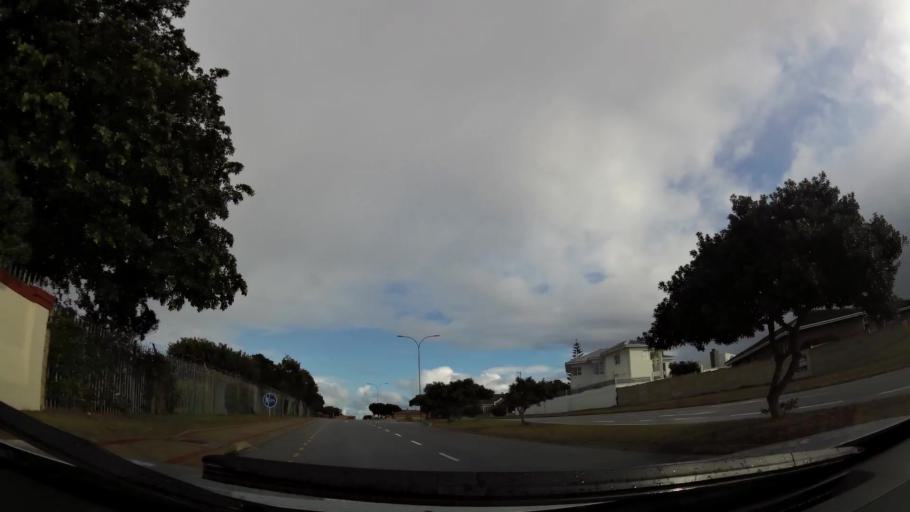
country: ZA
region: Western Cape
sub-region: Eden District Municipality
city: Mossel Bay
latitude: -34.1914
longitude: 22.1140
